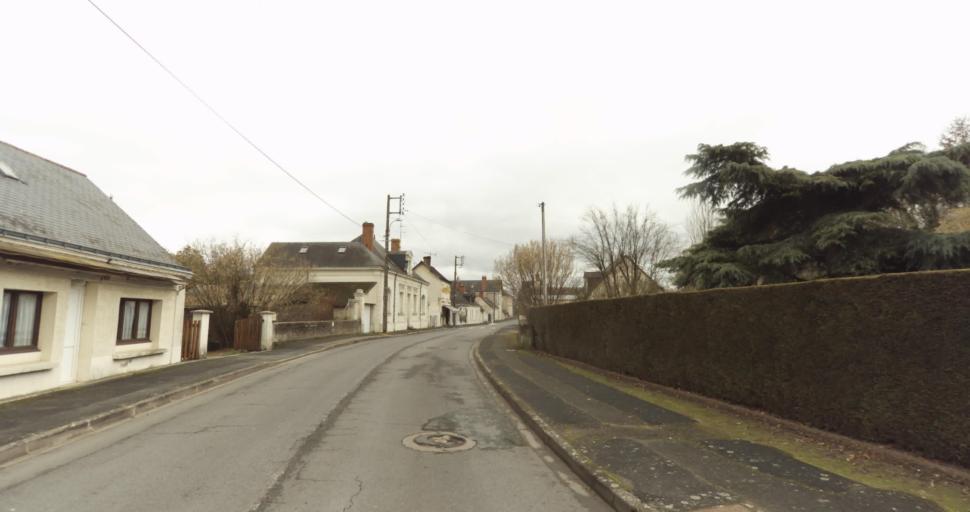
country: FR
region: Pays de la Loire
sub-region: Departement de Maine-et-Loire
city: Jumelles
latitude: 47.3858
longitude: -0.1144
